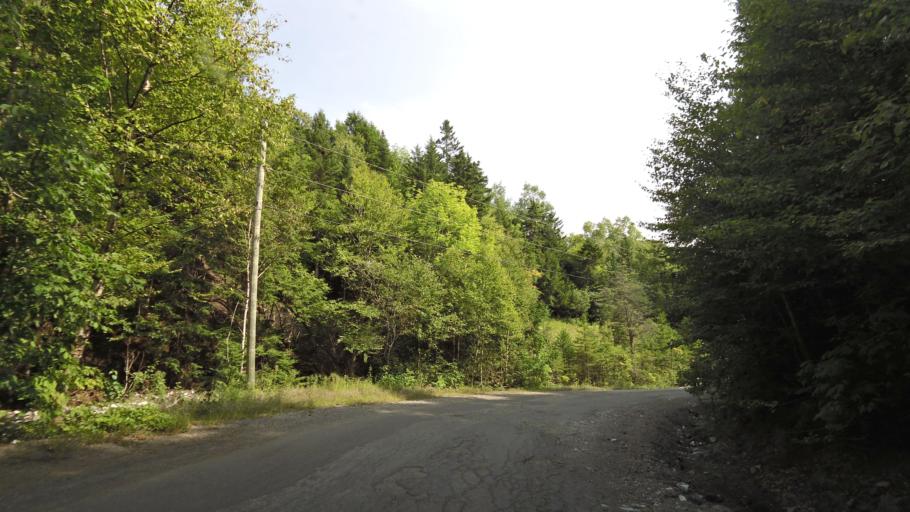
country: CA
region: New Brunswick
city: Hampton
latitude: 45.5521
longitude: -65.8386
